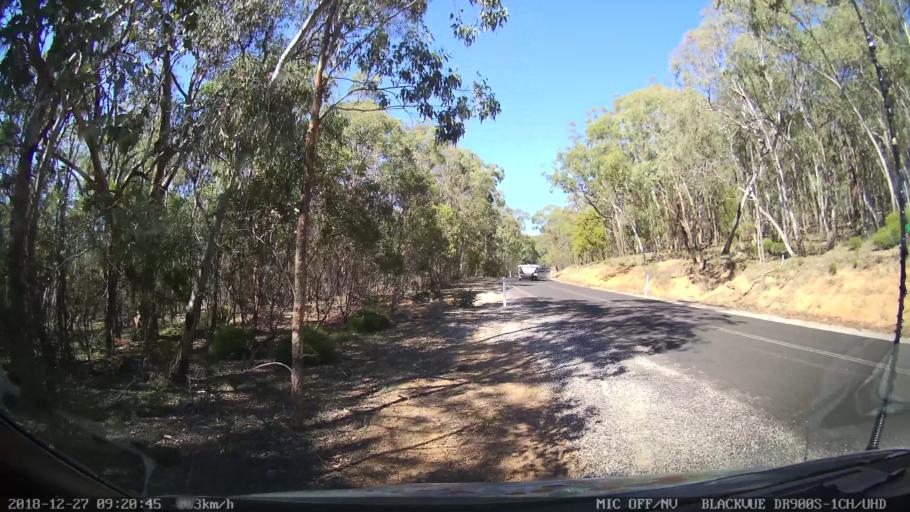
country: AU
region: New South Wales
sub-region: Lithgow
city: Portland
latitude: -33.1212
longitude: 150.0208
